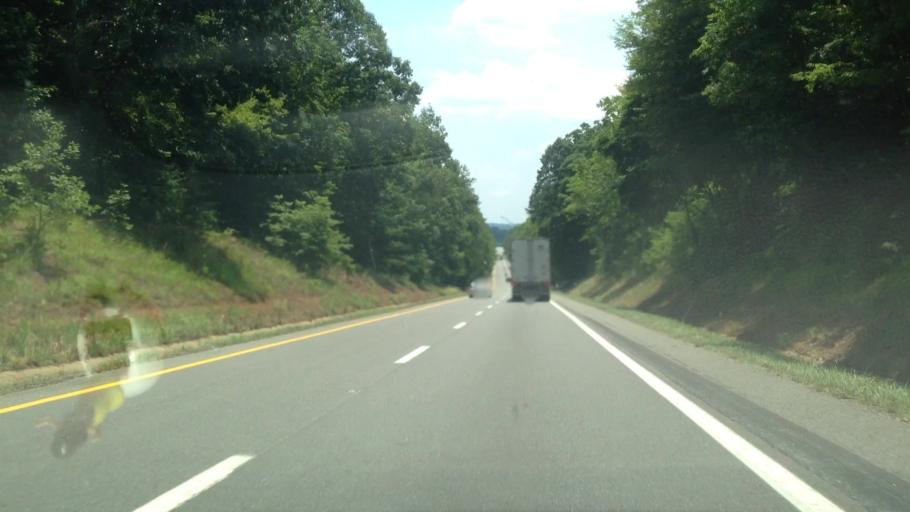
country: US
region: Virginia
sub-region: City of Martinsville
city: Martinsville
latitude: 36.6362
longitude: -79.8913
